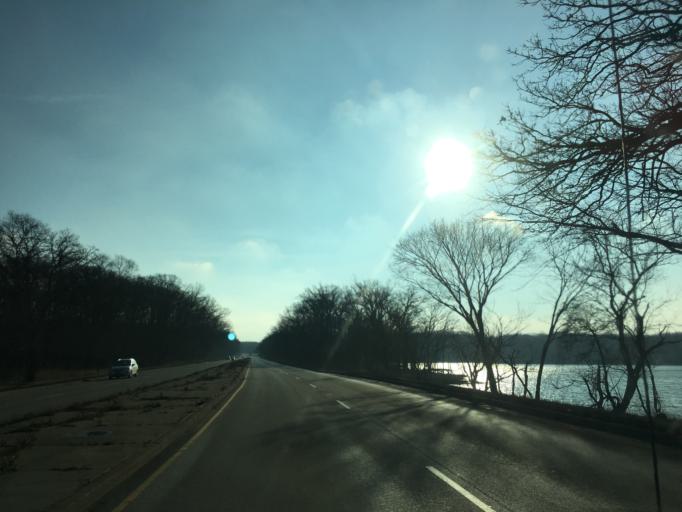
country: US
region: Illinois
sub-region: Cook County
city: Elk Grove Village
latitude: 42.0306
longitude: -88.0078
